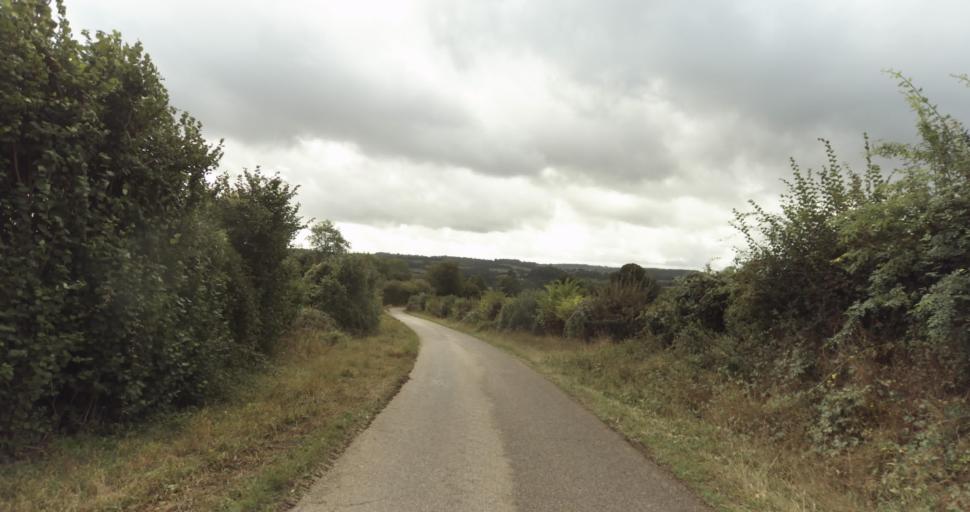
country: FR
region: Lower Normandy
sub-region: Departement de l'Orne
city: Gace
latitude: 48.8745
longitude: 0.2713
